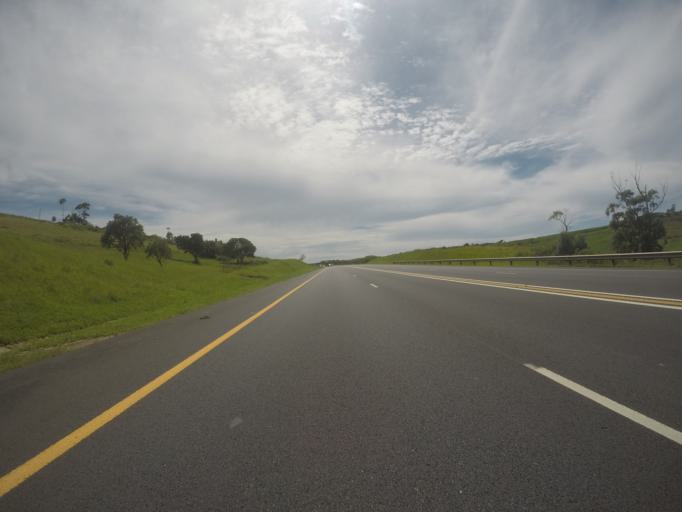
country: ZA
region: KwaZulu-Natal
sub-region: iLembe District Municipality
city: Mandeni
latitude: -29.1662
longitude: 31.5270
